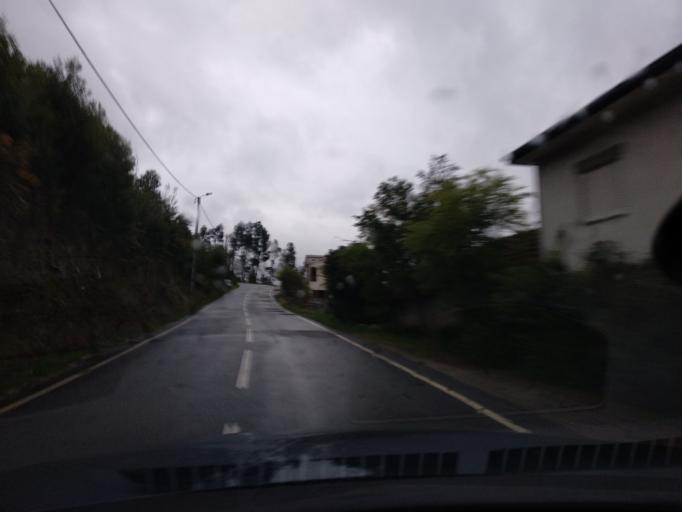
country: PT
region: Porto
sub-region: Penafiel
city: Penafiel
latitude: 41.1916
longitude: -8.2871
